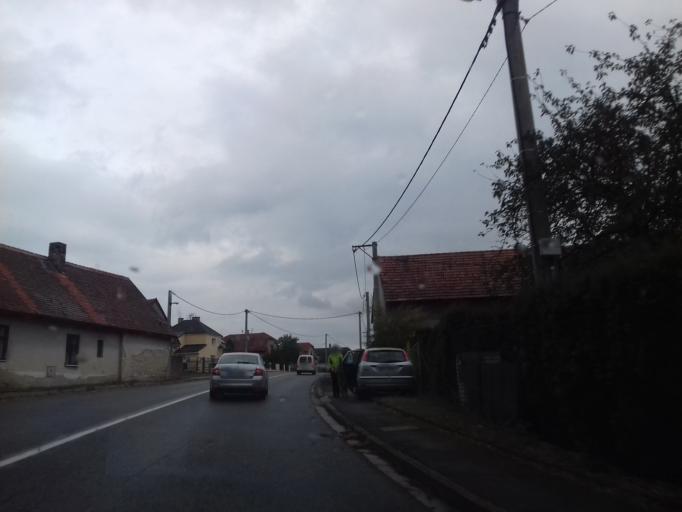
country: CZ
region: Pardubicky
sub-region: Okres Chrudim
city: Chrast
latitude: 49.8948
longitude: 15.9568
